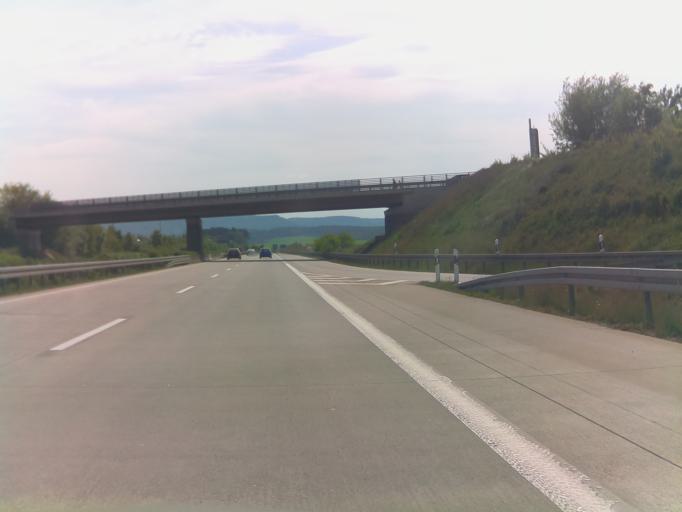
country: DE
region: Thuringia
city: Heilbad Heiligenstadt
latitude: 51.3979
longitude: 10.1323
